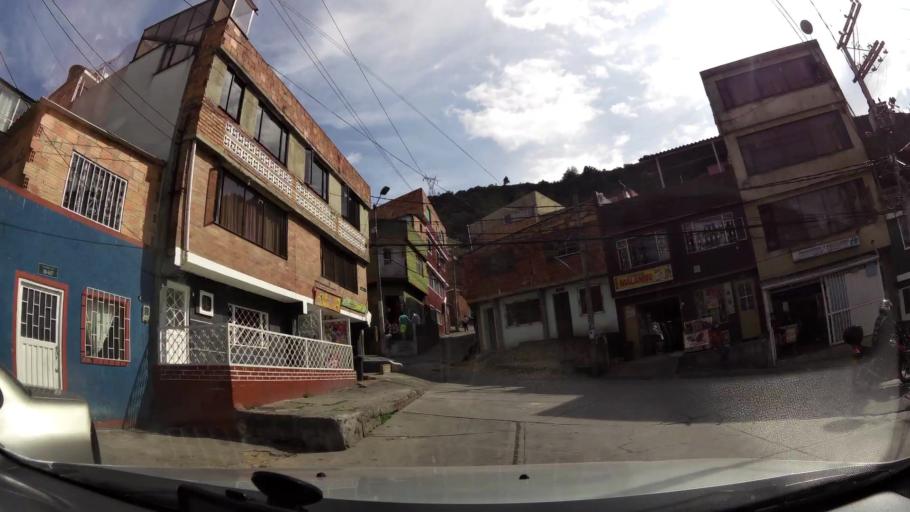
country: CO
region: Bogota D.C.
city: Bogota
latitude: 4.5584
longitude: -74.1010
